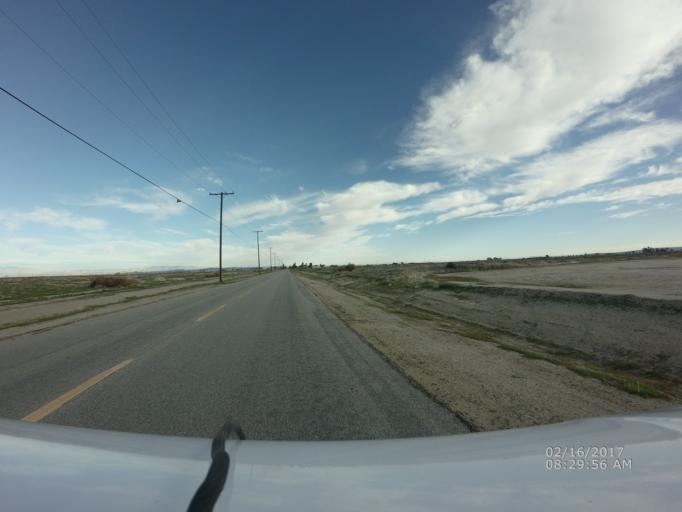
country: US
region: California
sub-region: Los Angeles County
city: Lancaster
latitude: 34.6989
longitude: -118.0054
